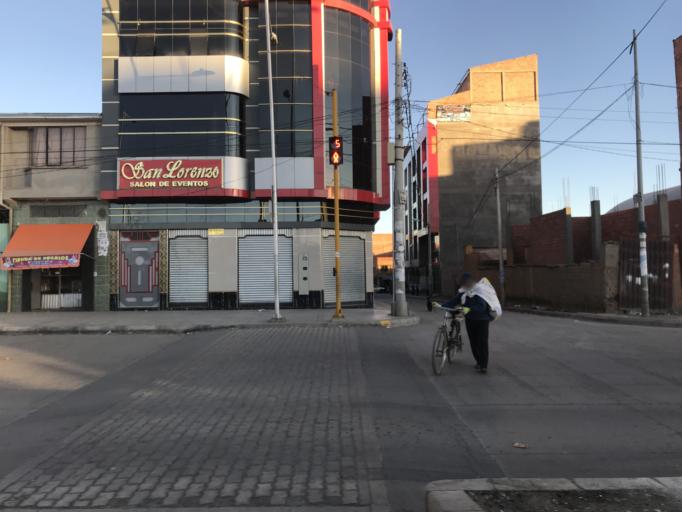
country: BO
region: La Paz
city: La Paz
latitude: -16.4935
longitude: -68.2172
